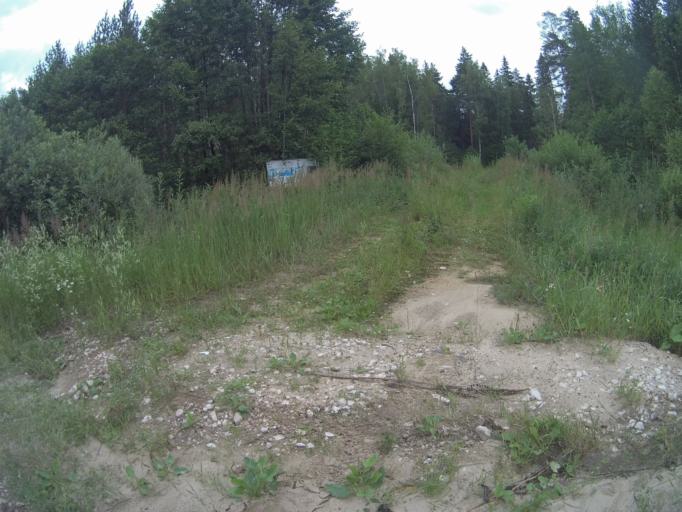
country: RU
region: Vladimir
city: Orgtrud
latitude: 55.9981
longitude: 40.6681
